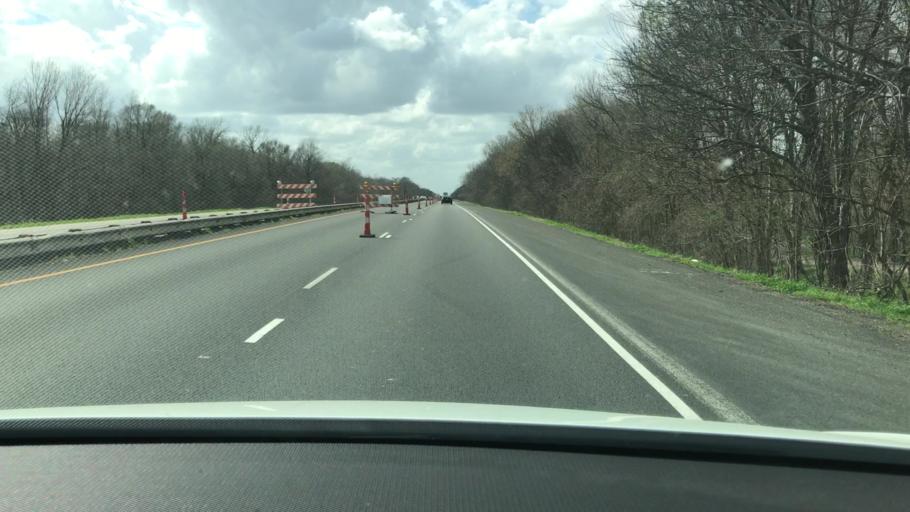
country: US
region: Louisiana
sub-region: Saint Landry Parish
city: Krotz Springs
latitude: 30.5568
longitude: -91.6587
